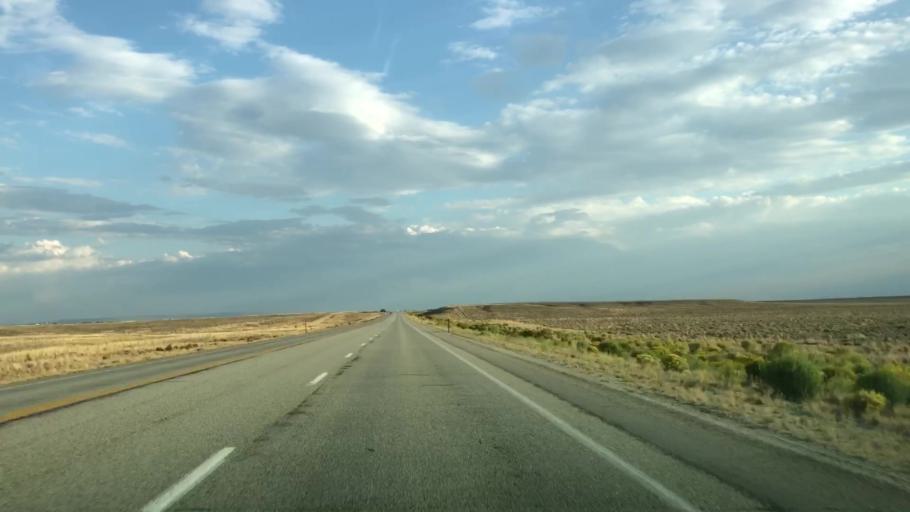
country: US
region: Wyoming
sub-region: Sweetwater County
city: North Rock Springs
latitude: 42.1835
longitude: -109.4781
